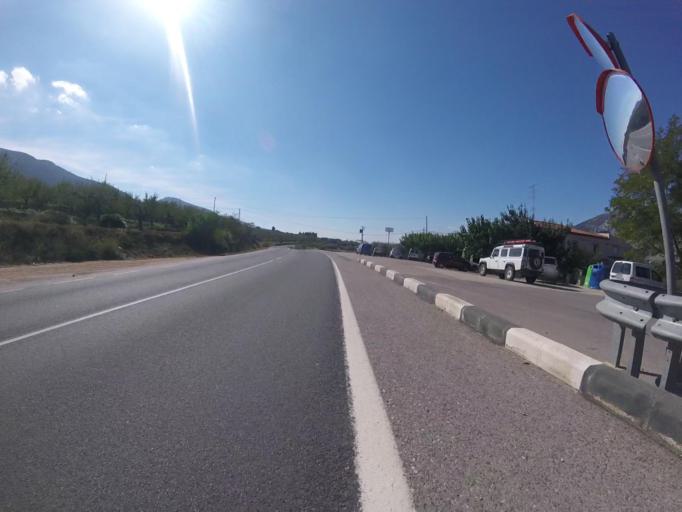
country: ES
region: Valencia
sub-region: Provincia de Castello
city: Sierra-Engarceran
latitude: 40.3065
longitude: -0.0411
